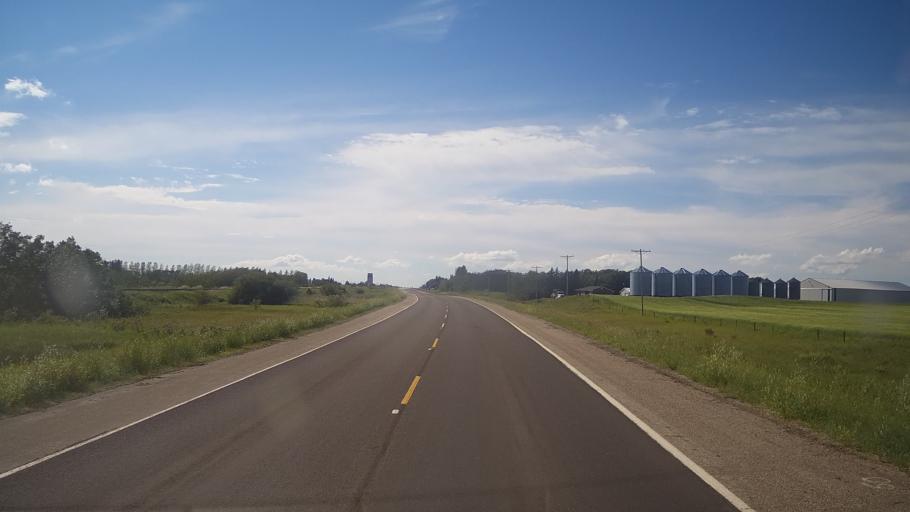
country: CA
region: Saskatchewan
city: Foam Lake
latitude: 51.2575
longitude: -103.7197
